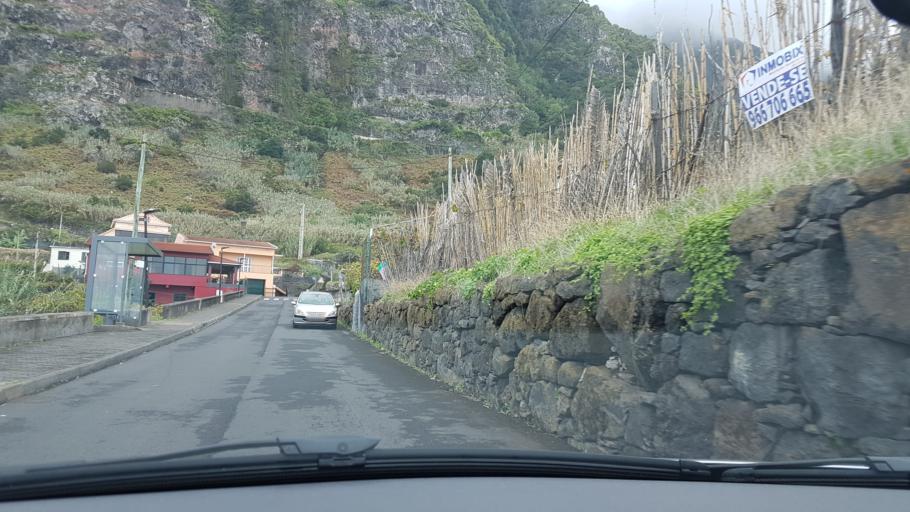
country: PT
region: Madeira
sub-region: Sao Vicente
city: Sao Vicente
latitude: 32.8275
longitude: -16.9852
